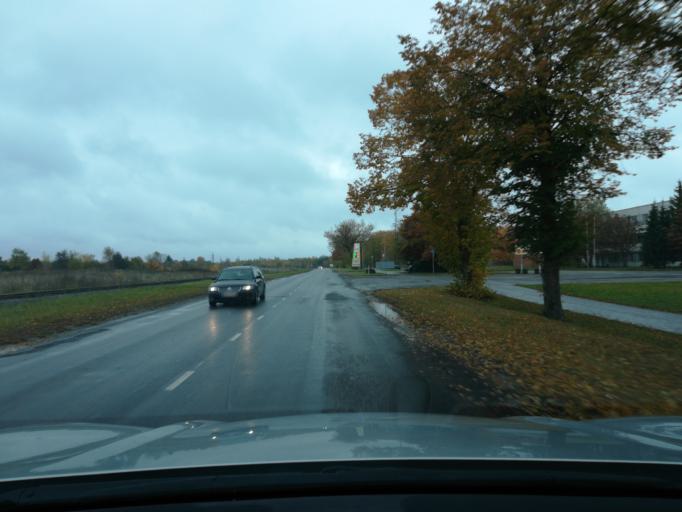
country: EE
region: Ida-Virumaa
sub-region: Johvi vald
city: Johvi
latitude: 59.3208
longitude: 27.4269
